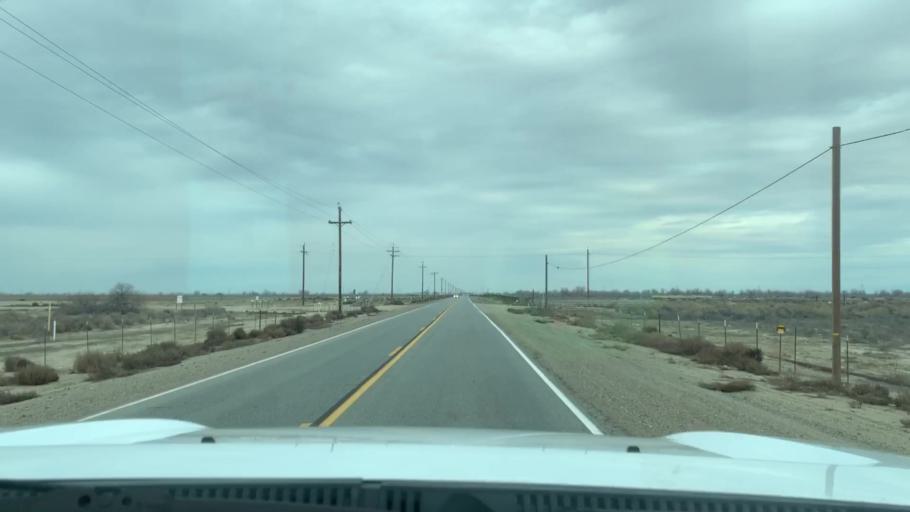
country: US
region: California
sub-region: Kern County
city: Rosedale
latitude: 35.3240
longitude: -119.2524
